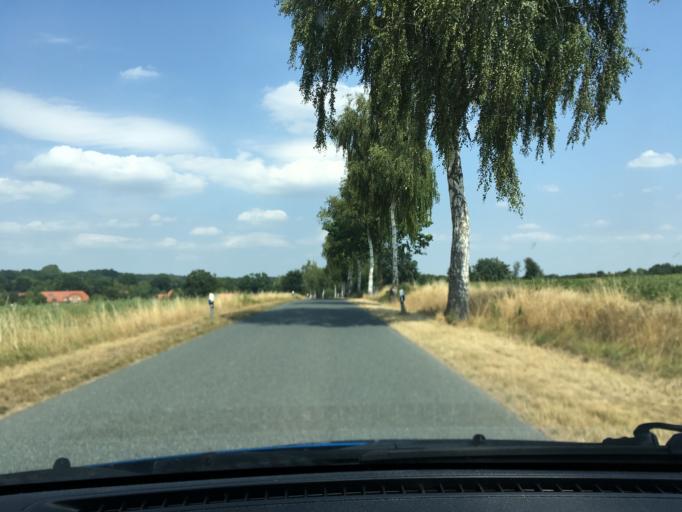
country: DE
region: Lower Saxony
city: Bienenbuttel
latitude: 53.1305
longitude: 10.4307
